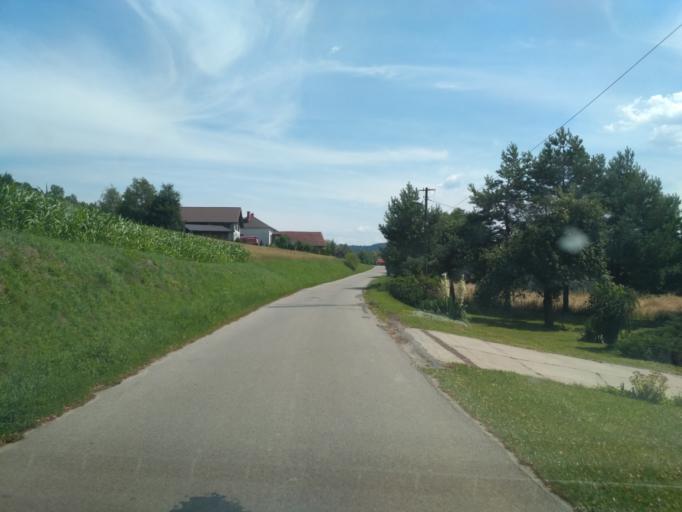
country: PL
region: Subcarpathian Voivodeship
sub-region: Powiat strzyzowski
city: Strzyzow
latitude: 49.8453
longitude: 21.8219
